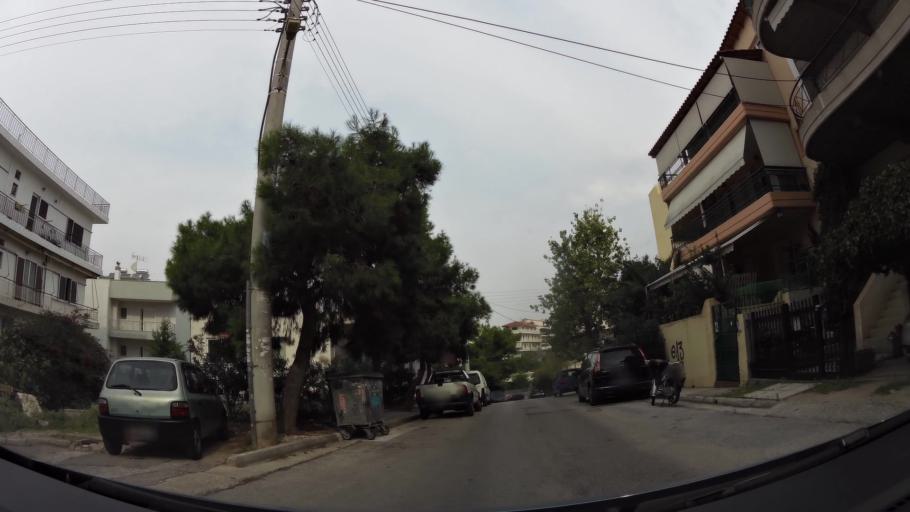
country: GR
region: Attica
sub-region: Nomarchia Athinas
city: Agios Dimitrios
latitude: 37.9296
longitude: 23.7341
